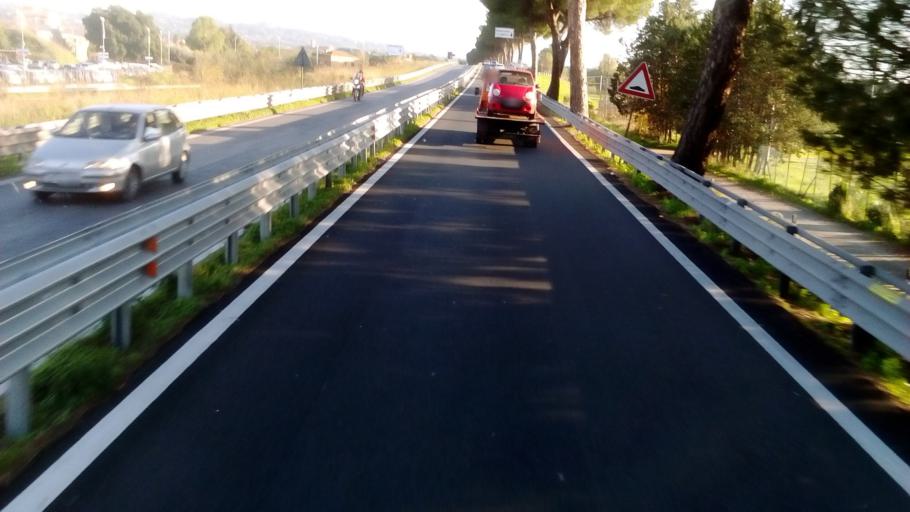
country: IT
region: Latium
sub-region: Citta metropolitana di Roma Capitale
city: Ciampino
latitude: 41.7795
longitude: 12.6045
